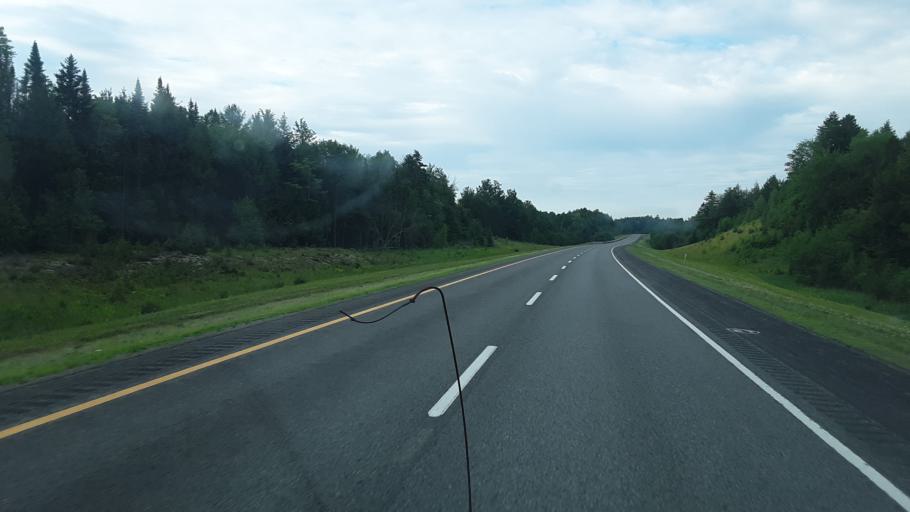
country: US
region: Maine
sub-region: Penobscot County
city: Medway
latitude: 45.6893
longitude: -68.4891
